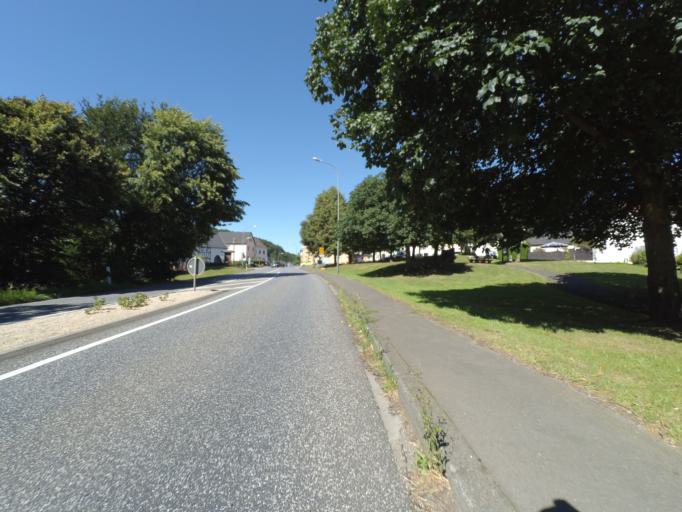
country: DE
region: Rheinland-Pfalz
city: Pelm
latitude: 50.2334
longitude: 6.6910
